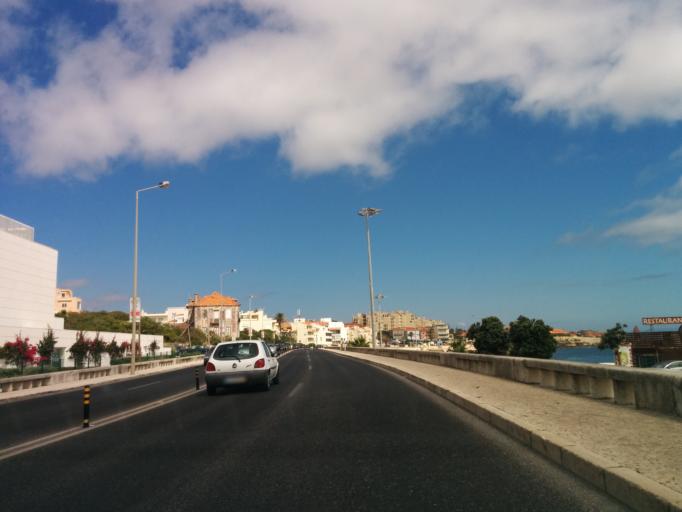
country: PT
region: Lisbon
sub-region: Cascais
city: Parede
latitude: 38.6863
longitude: -9.3567
